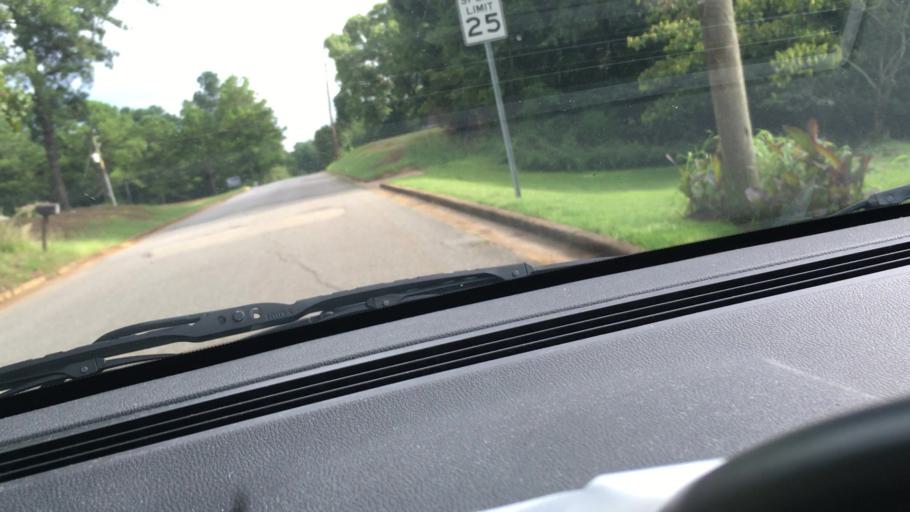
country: US
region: Alabama
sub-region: Tuscaloosa County
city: Northport
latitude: 33.2441
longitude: -87.5846
